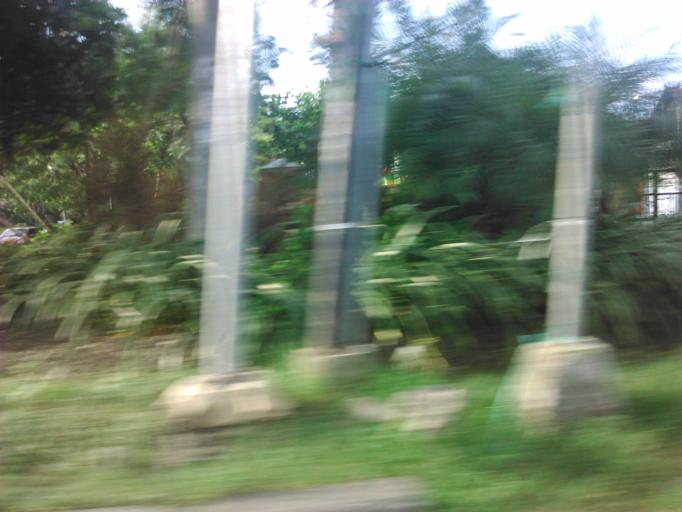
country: ID
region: East Java
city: Semampir
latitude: -7.2894
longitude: 112.7808
